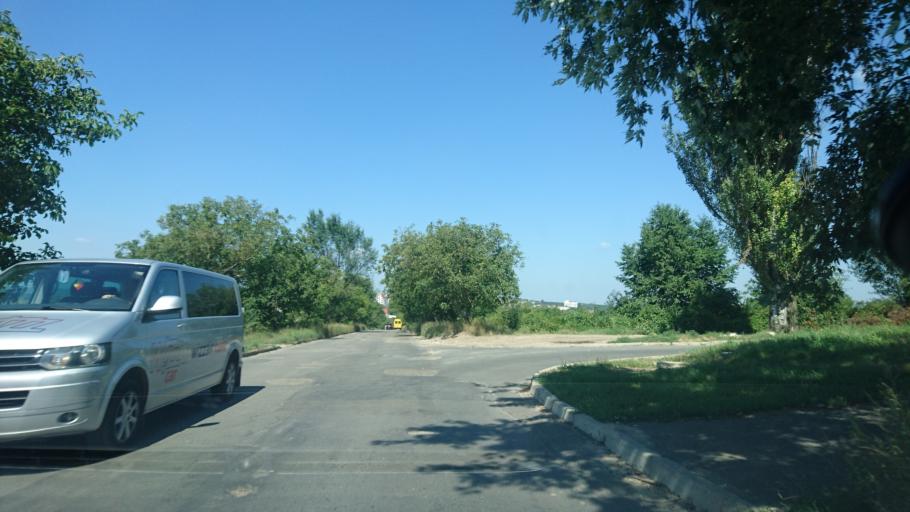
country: MD
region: Laloveni
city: Ialoveni
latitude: 47.0025
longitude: 28.7748
